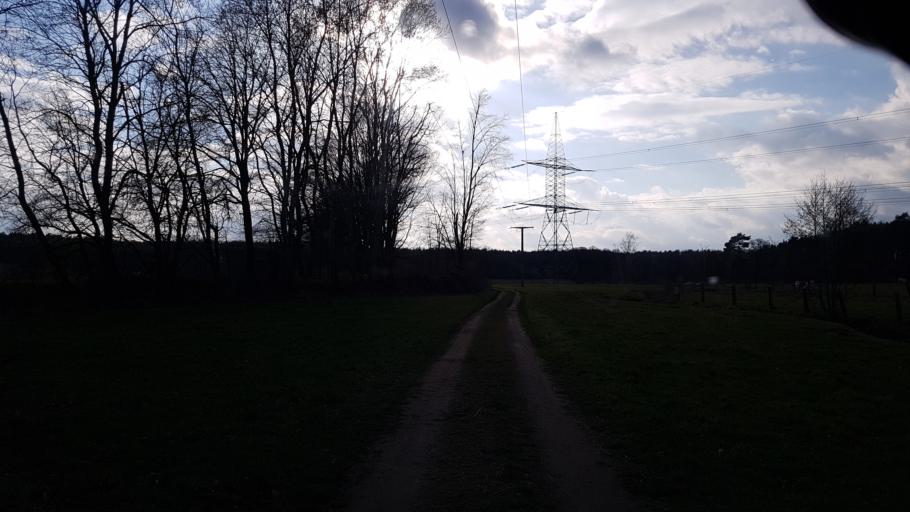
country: DE
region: Brandenburg
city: Bad Liebenwerda
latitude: 51.5391
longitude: 13.4331
